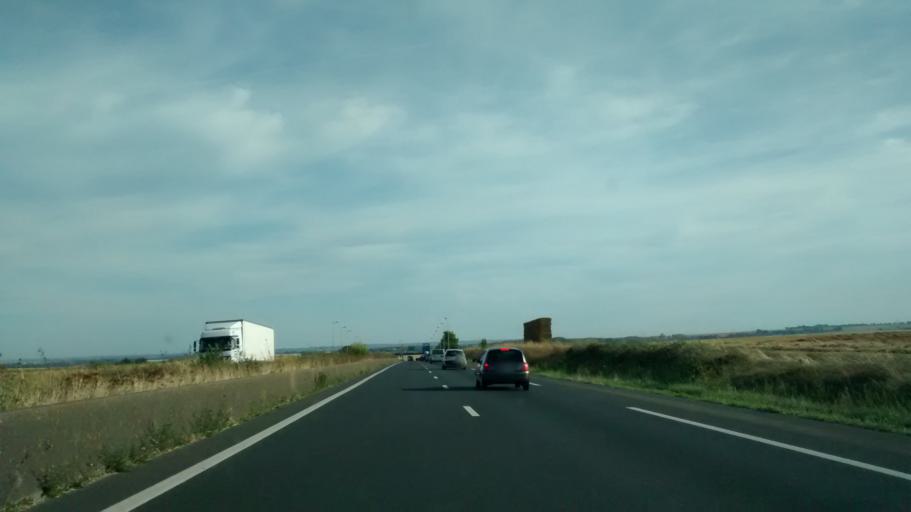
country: FR
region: Lower Normandy
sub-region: Departement du Calvados
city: Bretteville-sur-Odon
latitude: 49.1716
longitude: -0.4297
